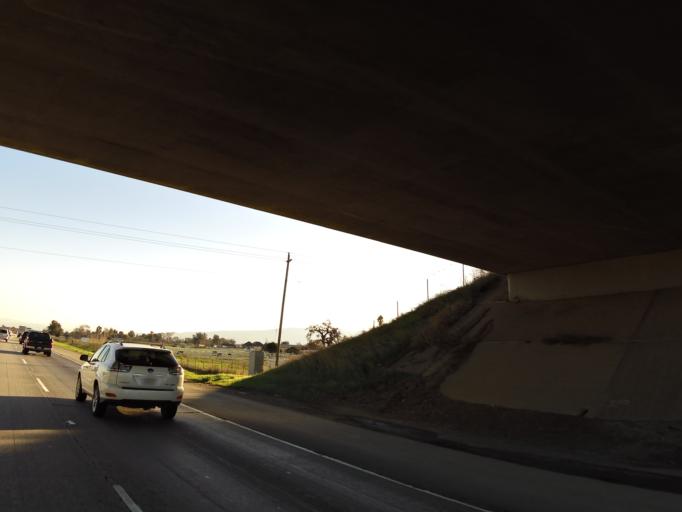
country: US
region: California
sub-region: Santa Clara County
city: San Martin
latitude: 37.0714
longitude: -121.5901
